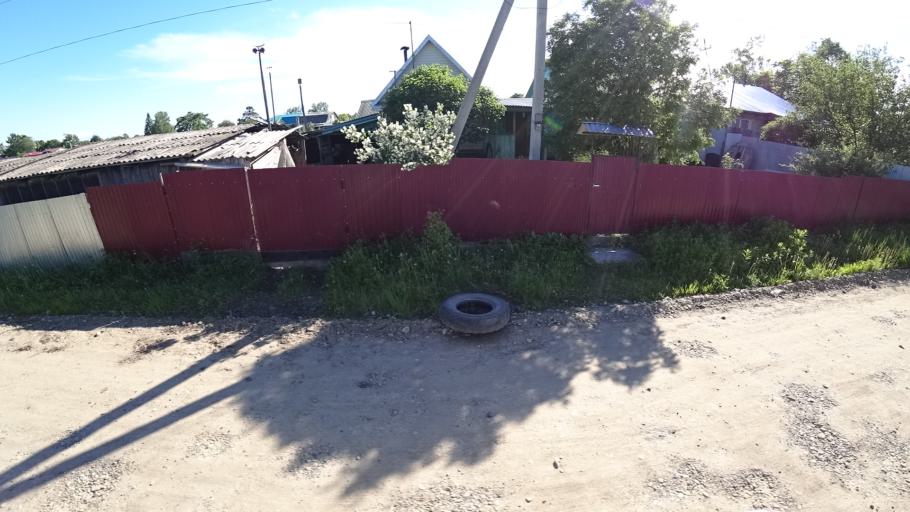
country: RU
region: Khabarovsk Krai
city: Khor
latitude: 47.8903
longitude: 134.9920
